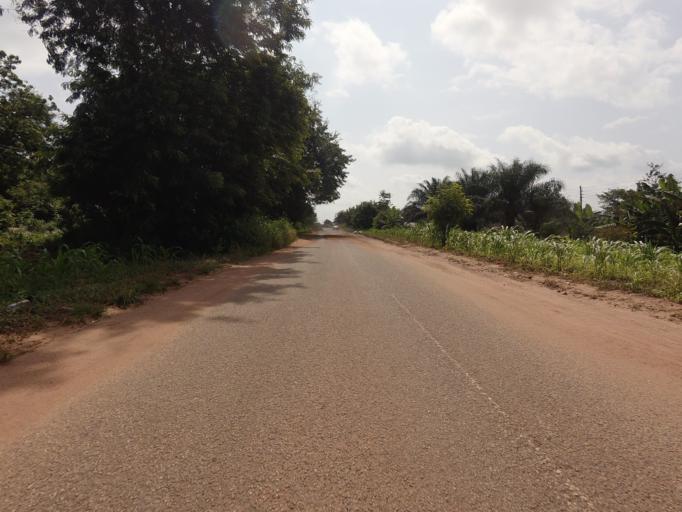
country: TG
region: Maritime
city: Lome
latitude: 6.2660
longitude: 0.9517
